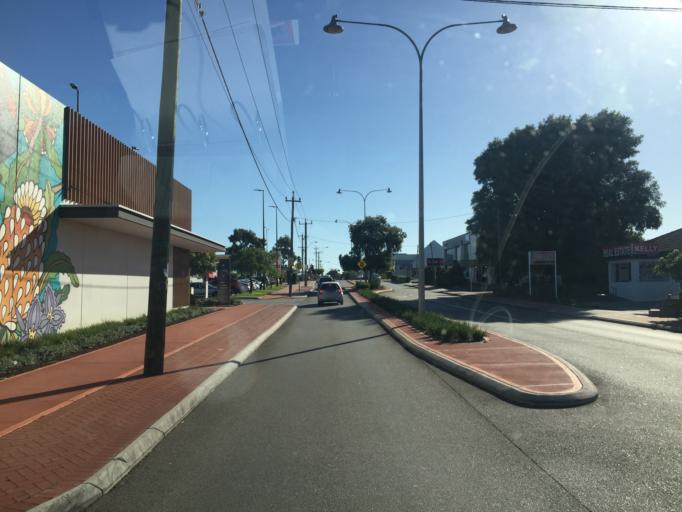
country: AU
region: Western Australia
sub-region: Belmont
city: Belmont
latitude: -31.9642
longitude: 115.9338
